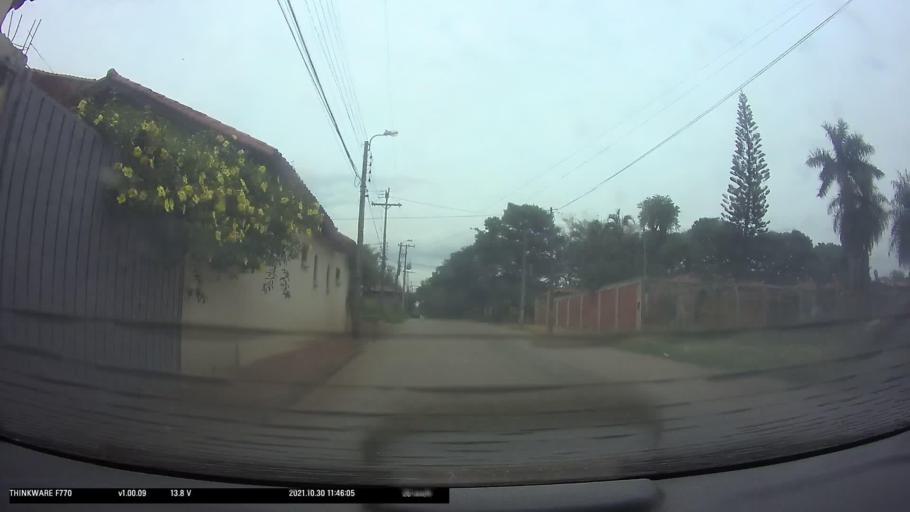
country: PY
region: Central
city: Fernando de la Mora
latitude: -25.3186
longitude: -57.5304
